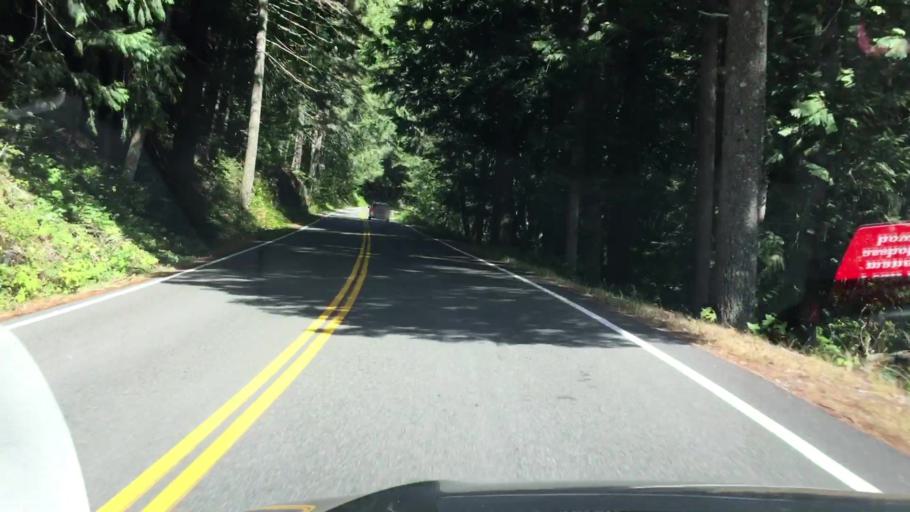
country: US
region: Washington
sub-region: Pierce County
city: Eatonville
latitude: 46.7387
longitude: -121.9099
